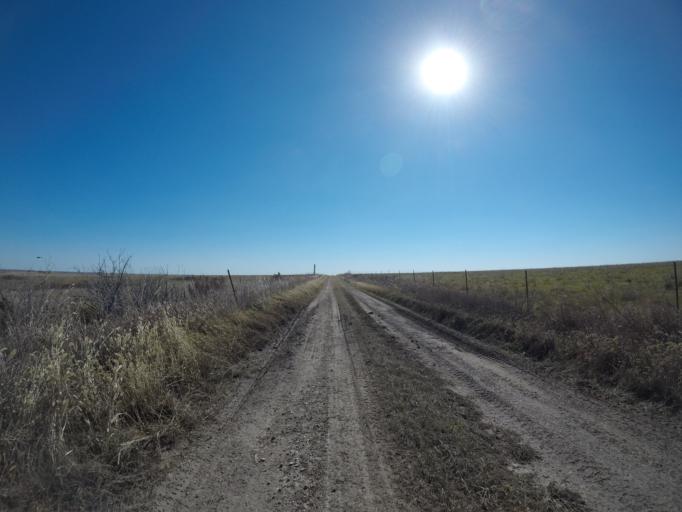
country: US
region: Kansas
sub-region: Wabaunsee County
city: Alma
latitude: 38.9915
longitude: -96.4642
